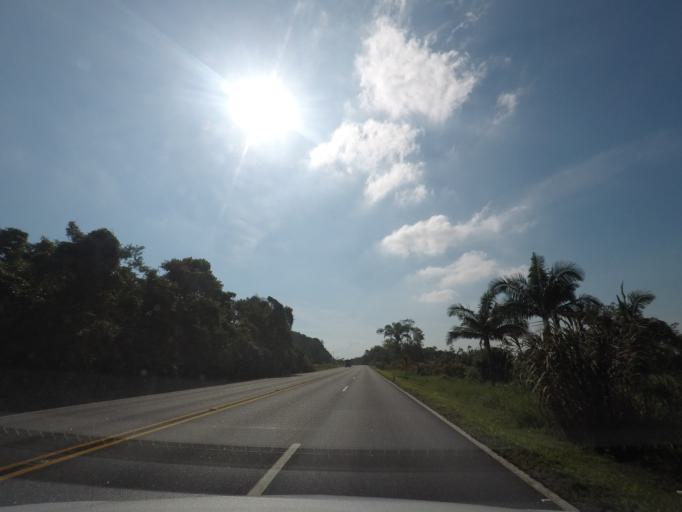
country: BR
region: Parana
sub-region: Pontal Do Parana
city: Pontal do Parana
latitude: -25.6323
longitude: -48.5945
